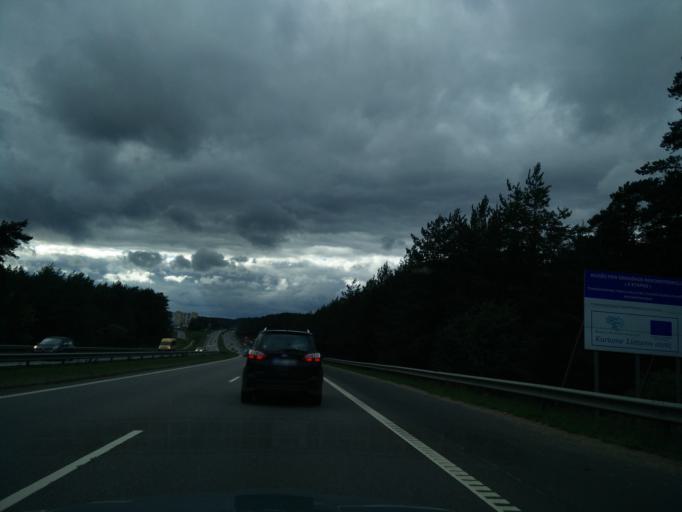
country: LT
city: Grigiskes
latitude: 54.6661
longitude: 25.1189
